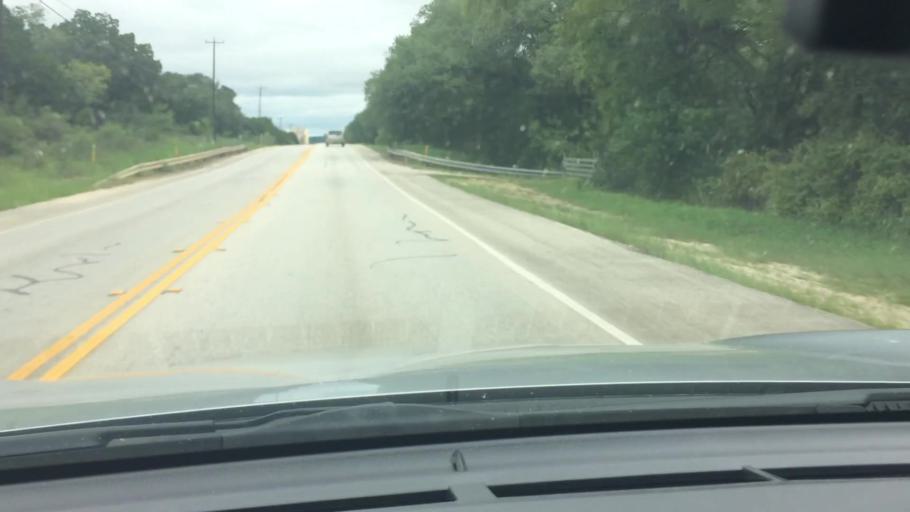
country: US
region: Texas
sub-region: Bexar County
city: Live Oak
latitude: 29.6124
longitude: -98.3641
